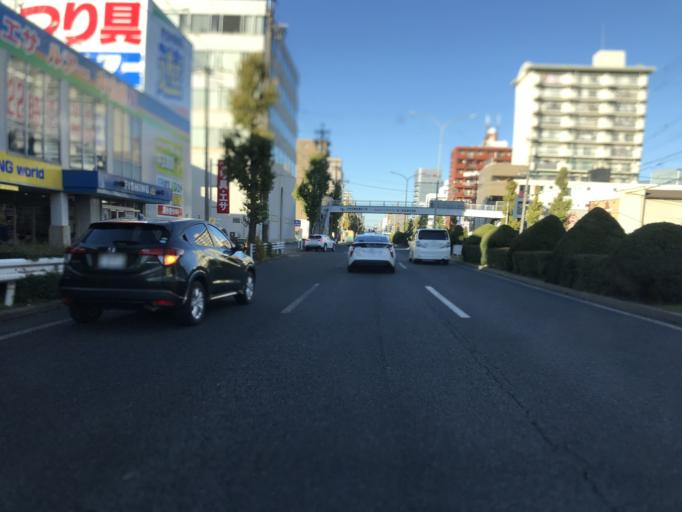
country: JP
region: Aichi
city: Nagoya-shi
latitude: 35.1592
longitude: 136.8708
